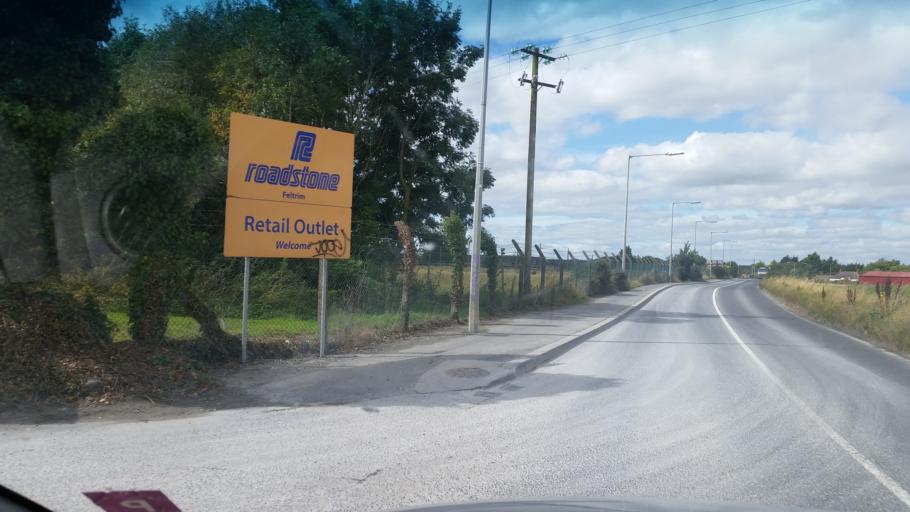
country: IE
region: Leinster
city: Kinsealy-Drinan
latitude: 53.4394
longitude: -6.1920
